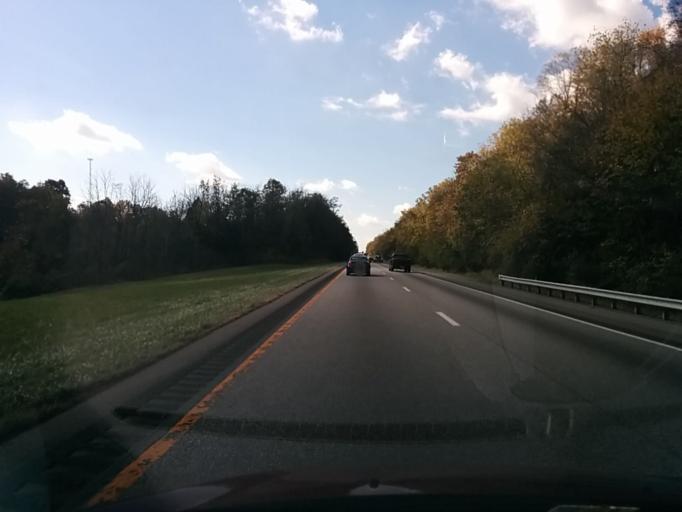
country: US
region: Virginia
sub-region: Botetourt County
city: Daleville
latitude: 37.4320
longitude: -79.8738
